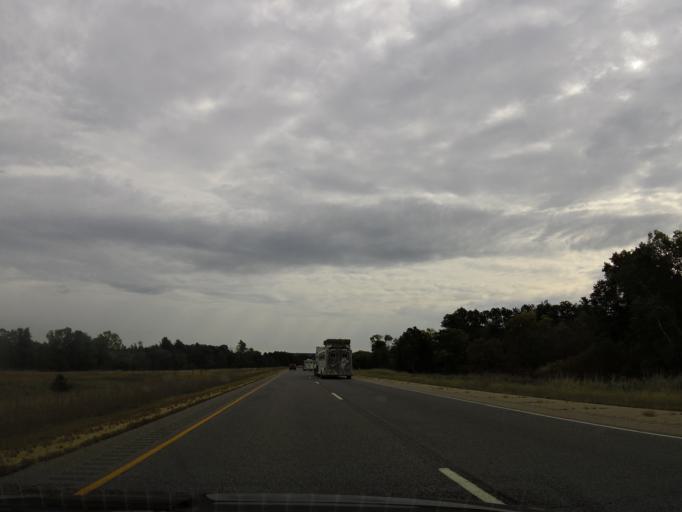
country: US
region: Wisconsin
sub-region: Monroe County
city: Sparta
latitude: 43.9431
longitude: -90.6867
